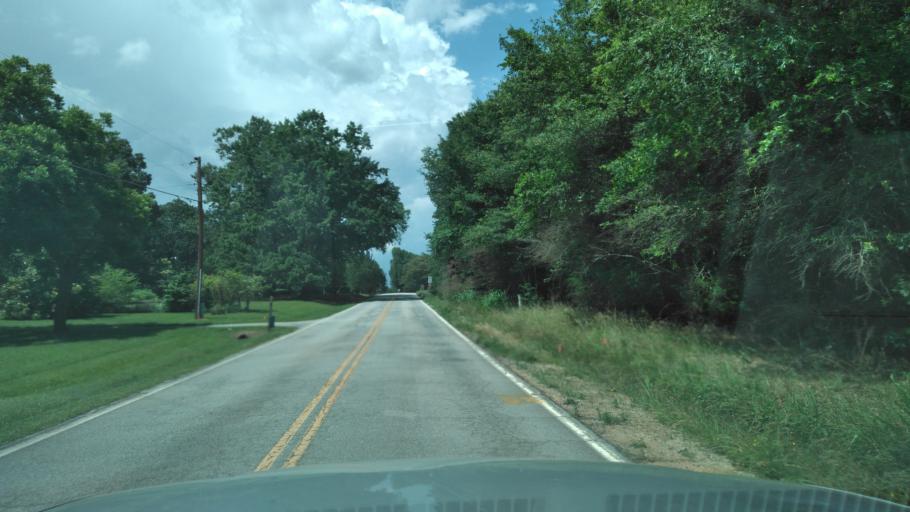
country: US
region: South Carolina
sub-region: Laurens County
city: Laurens
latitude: 34.5129
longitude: -82.0939
